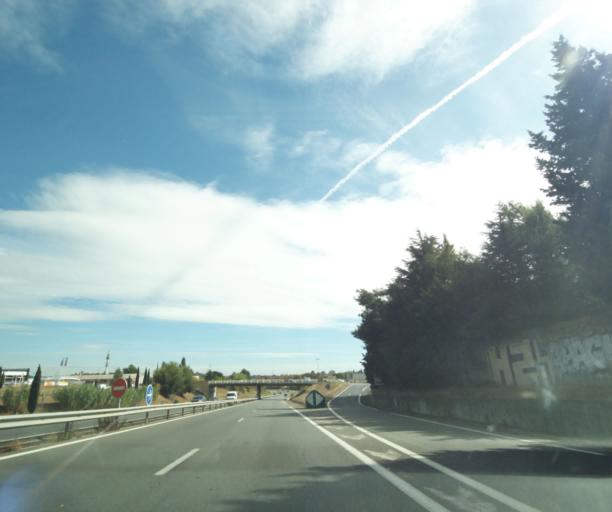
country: FR
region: Languedoc-Roussillon
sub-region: Departement de l'Herault
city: Juvignac
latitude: 43.6112
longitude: 3.8021
